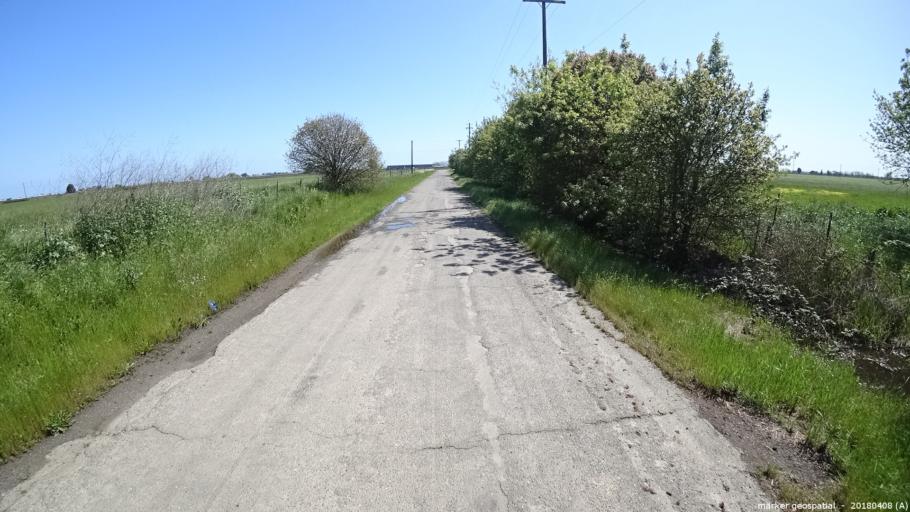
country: US
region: California
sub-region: San Joaquin County
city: Thornton
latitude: 38.2986
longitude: -121.4449
